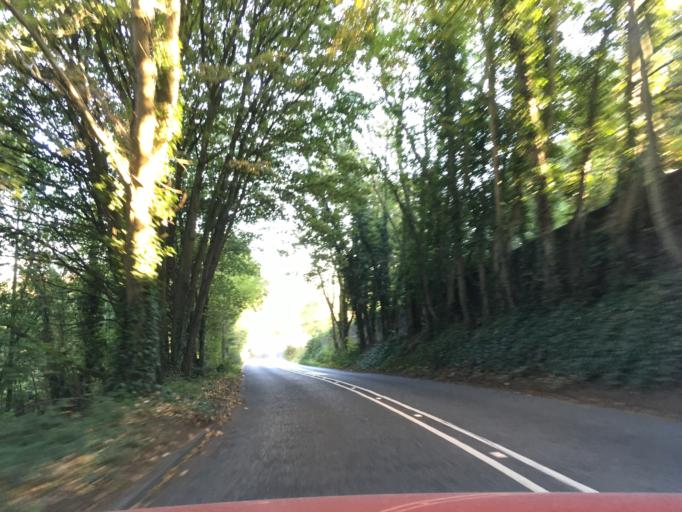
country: GB
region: England
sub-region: Bristol
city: Bristol
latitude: 51.4500
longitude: -2.6278
